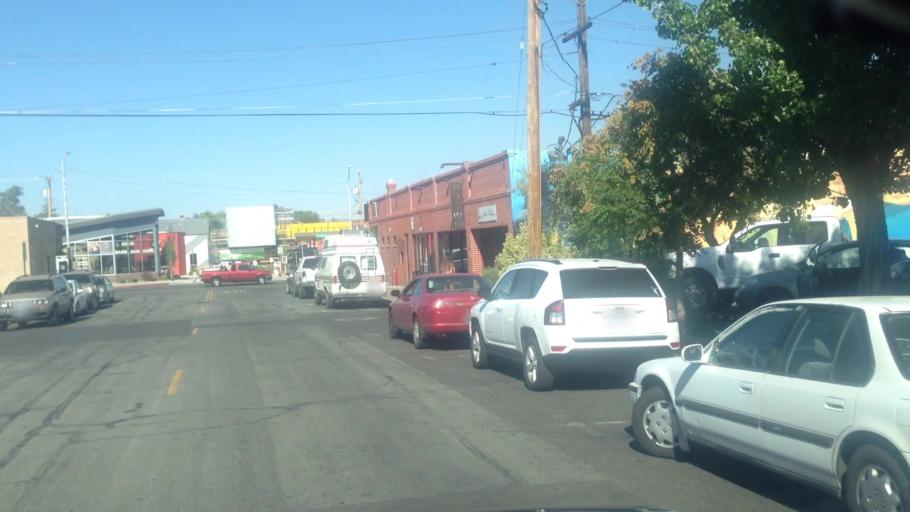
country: US
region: Nevada
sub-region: Washoe County
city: Reno
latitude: 39.5181
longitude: -119.8102
